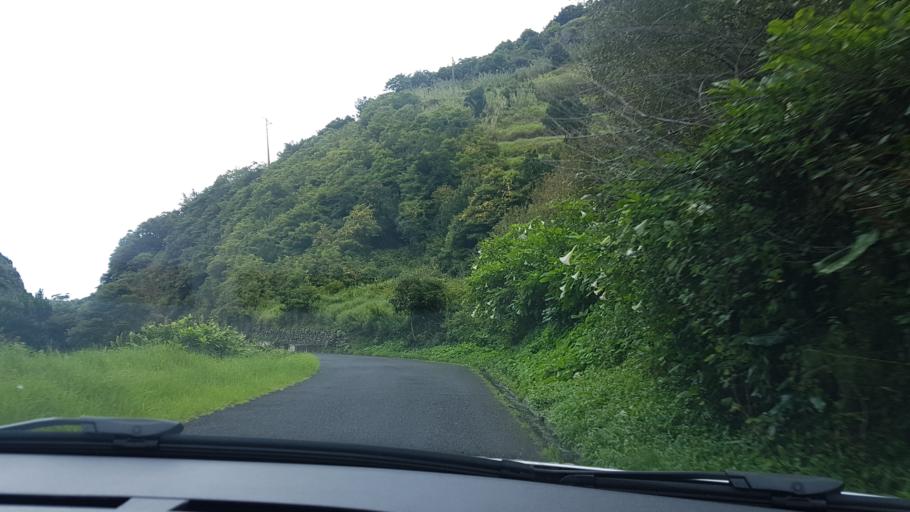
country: PT
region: Madeira
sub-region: Sao Vicente
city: Sao Vicente
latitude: 32.8215
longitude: -16.9755
